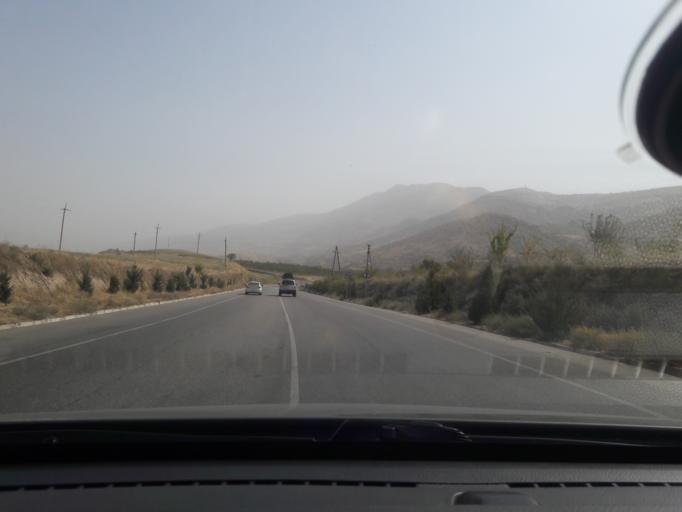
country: TJ
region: Republican Subordination
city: Vahdat
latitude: 38.4878
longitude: 69.1652
